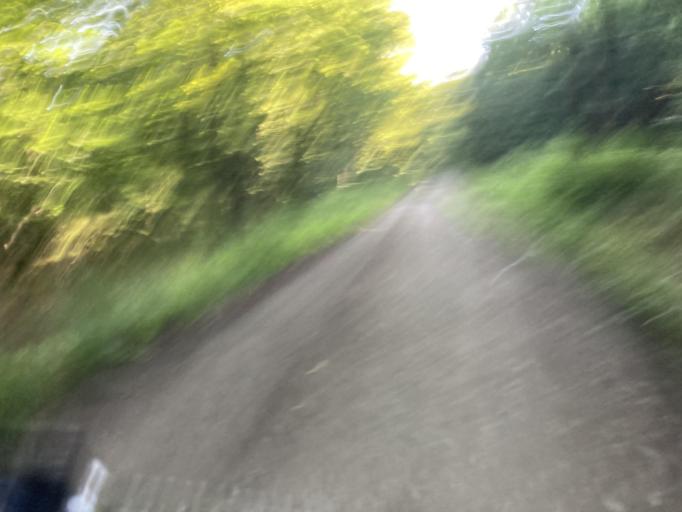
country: DE
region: Baden-Wuerttemberg
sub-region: Regierungsbezirk Stuttgart
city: Renningen
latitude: 48.7810
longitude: 8.9618
